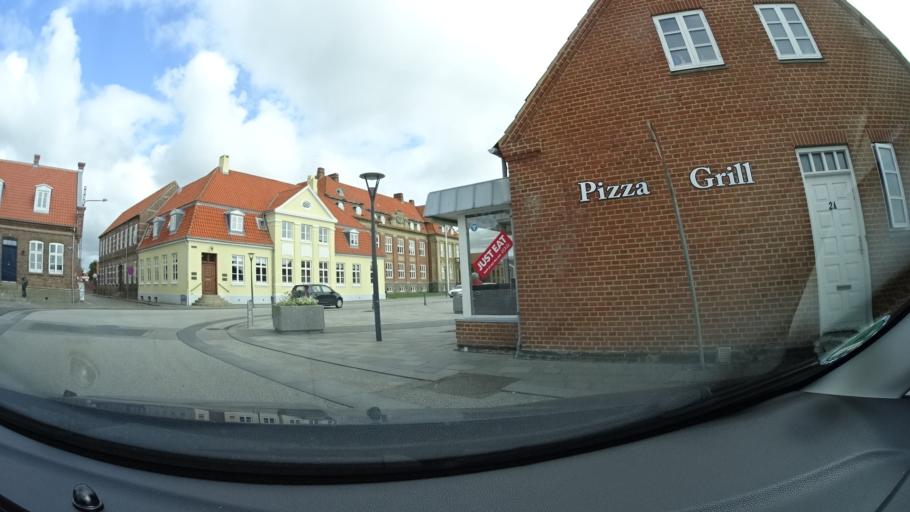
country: DK
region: Central Jutland
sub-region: Ringkobing-Skjern Kommune
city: Ringkobing
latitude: 56.0885
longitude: 8.2463
